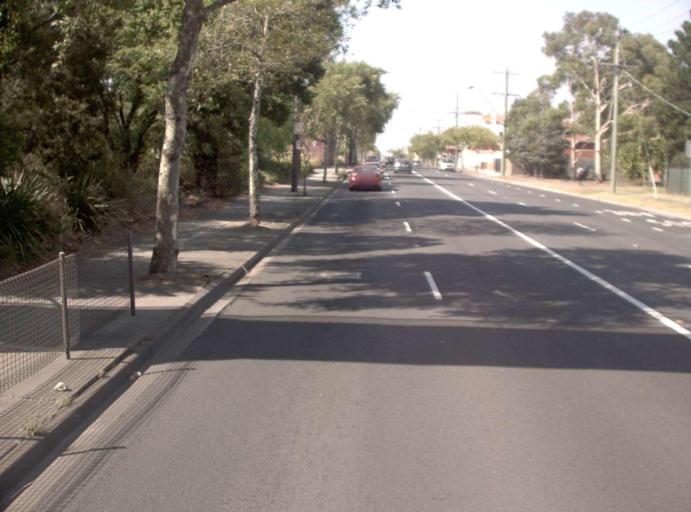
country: AU
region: Victoria
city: Hughesdale
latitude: -37.8949
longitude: 145.0879
